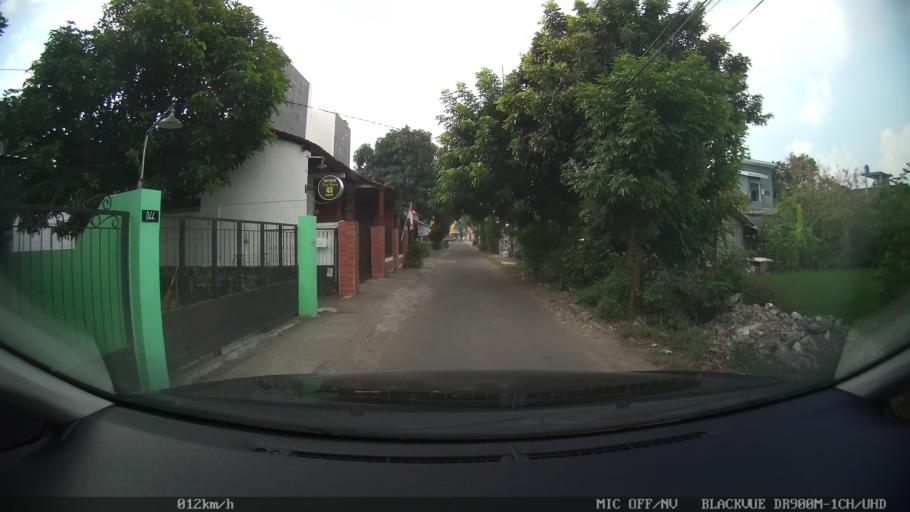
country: ID
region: Daerah Istimewa Yogyakarta
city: Yogyakarta
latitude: -7.8148
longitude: 110.4062
